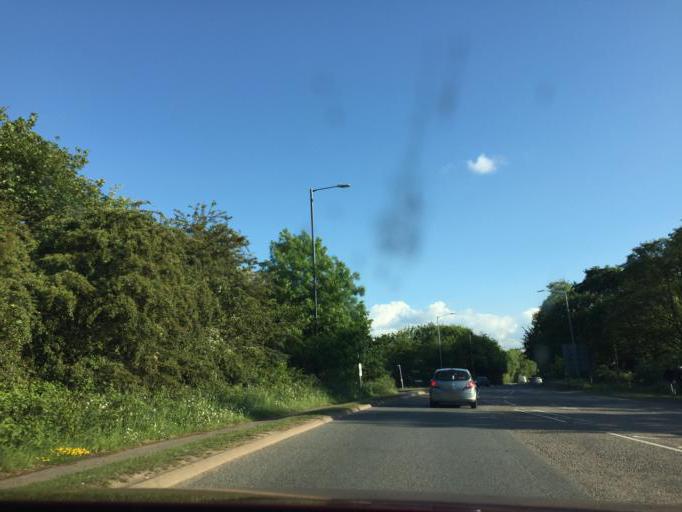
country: GB
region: England
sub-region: Warwickshire
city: Bedworth
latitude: 52.4973
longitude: -1.4723
